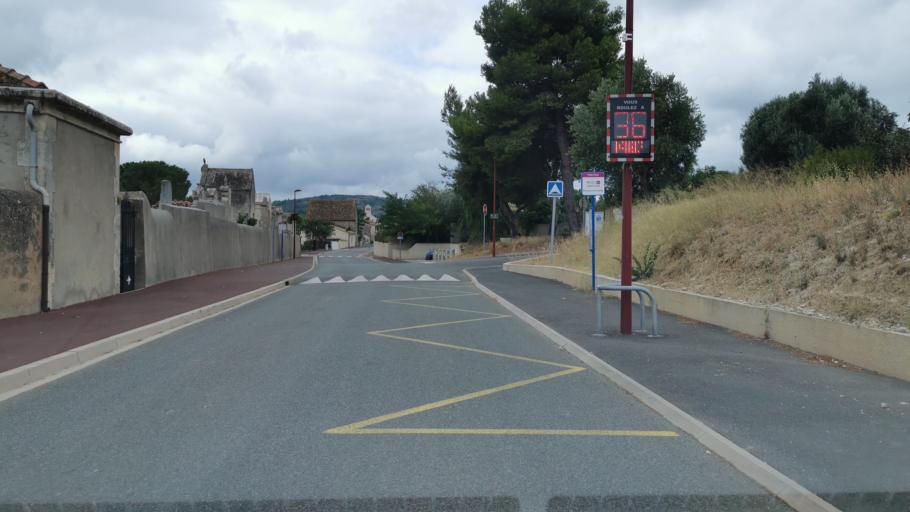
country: FR
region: Languedoc-Roussillon
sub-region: Departement de l'Aude
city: Nevian
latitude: 43.1946
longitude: 2.9293
